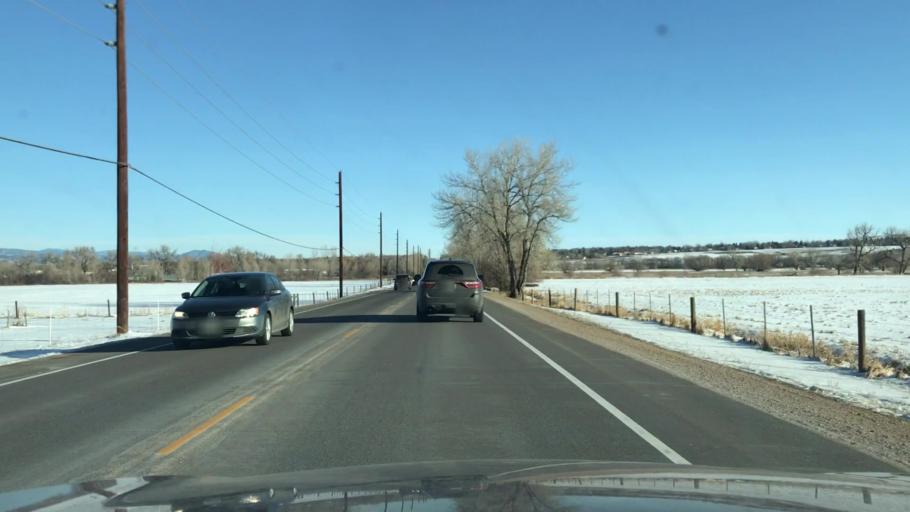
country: US
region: Colorado
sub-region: Boulder County
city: Gunbarrel
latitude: 40.0369
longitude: -105.1784
